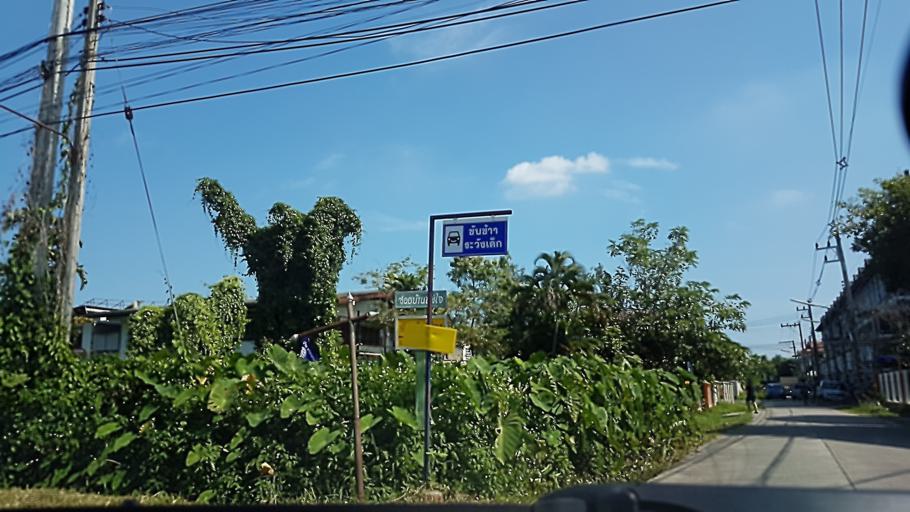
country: TH
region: Chiang Mai
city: Chiang Mai
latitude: 18.8428
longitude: 98.9765
